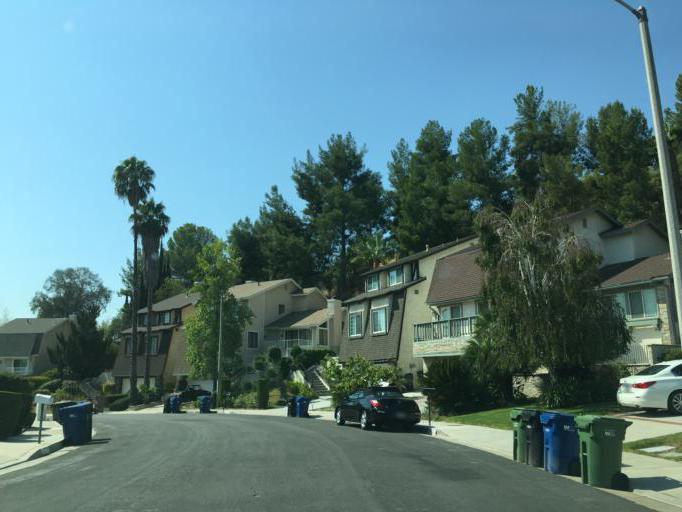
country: US
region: California
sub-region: Los Angeles County
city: West Hills
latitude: 34.1932
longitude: -118.6578
